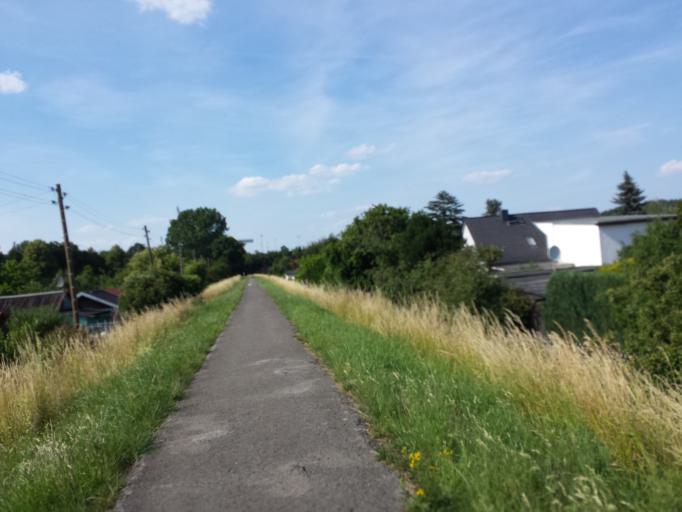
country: DE
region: Lower Saxony
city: Stuhr
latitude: 53.0931
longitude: 8.7449
